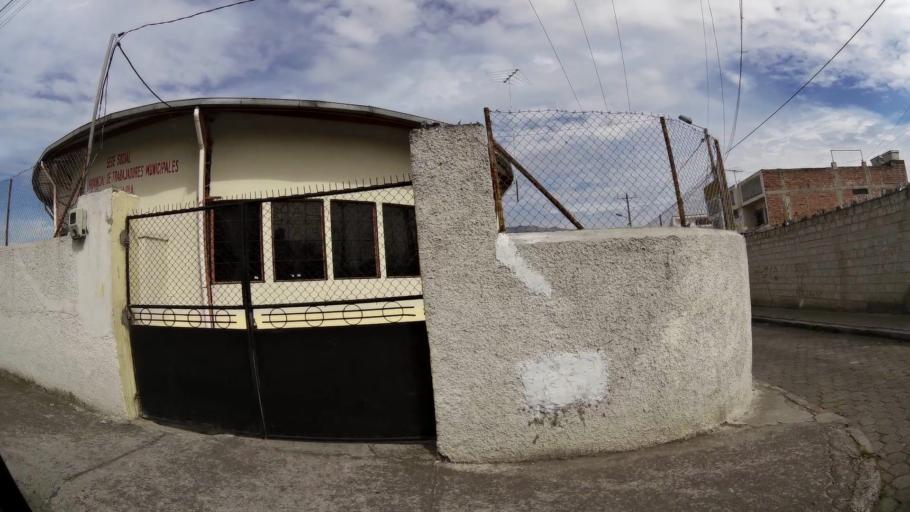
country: EC
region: Tungurahua
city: Ambato
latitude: -1.2480
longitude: -78.6277
